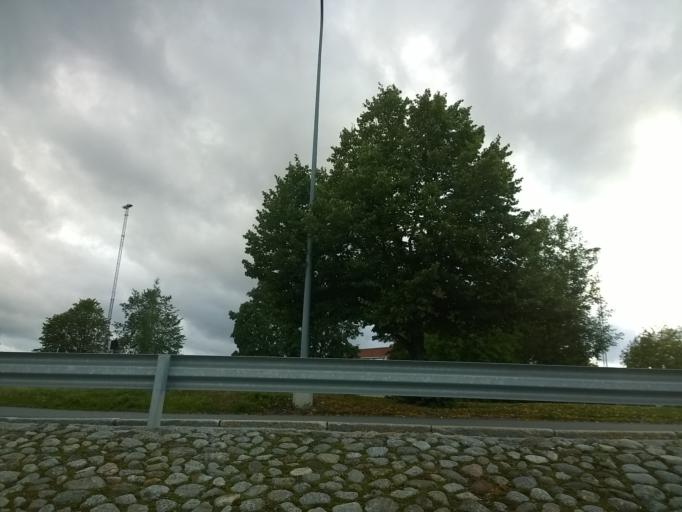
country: FI
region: Pirkanmaa
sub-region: Tampere
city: Tampere
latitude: 61.4899
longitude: 23.7796
